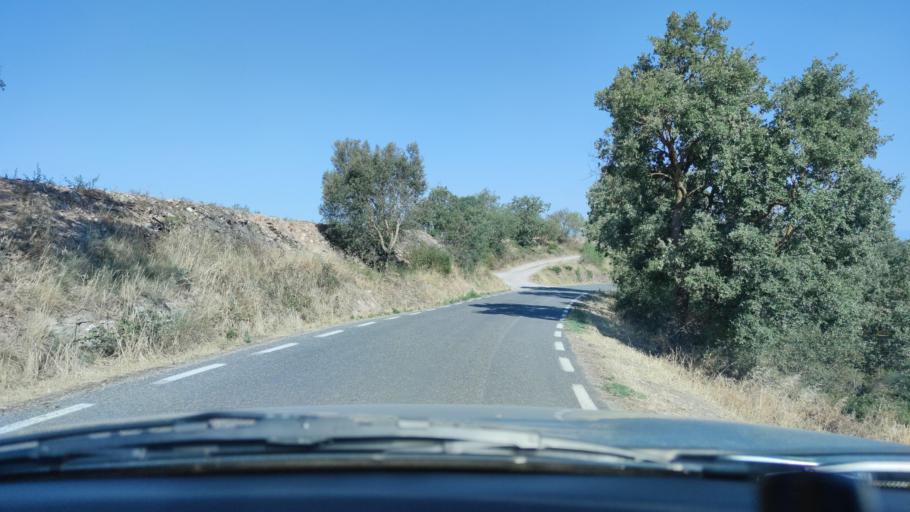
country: ES
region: Catalonia
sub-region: Provincia de Lleida
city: Ivorra
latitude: 41.7312
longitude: 1.3624
